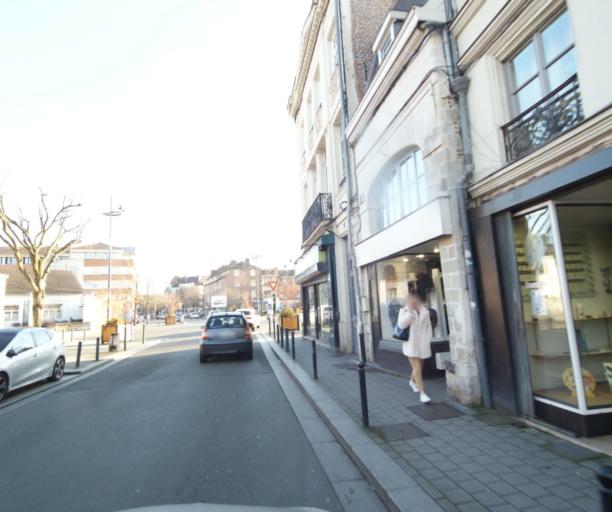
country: FR
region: Nord-Pas-de-Calais
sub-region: Departement du Nord
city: Valenciennes
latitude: 50.3609
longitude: 3.5230
